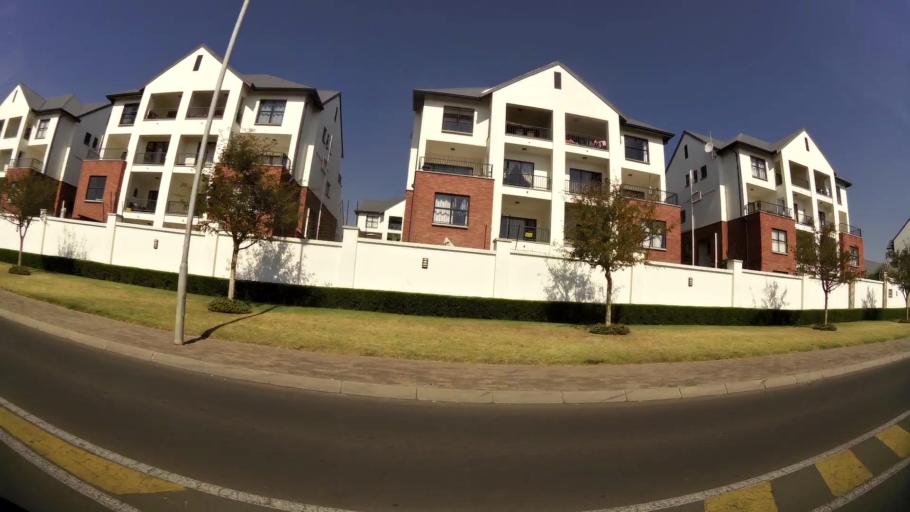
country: ZA
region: Gauteng
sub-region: City of Johannesburg Metropolitan Municipality
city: Modderfontein
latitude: -26.1177
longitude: 28.1604
